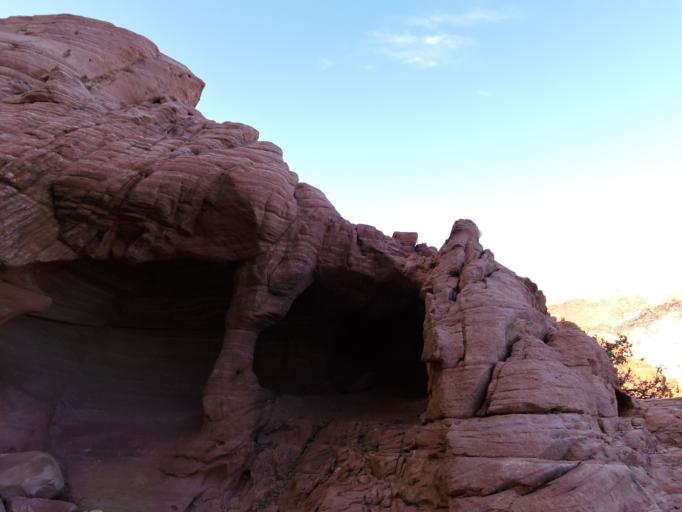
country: US
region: Nevada
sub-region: Clark County
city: Summerlin South
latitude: 36.1497
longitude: -115.4269
